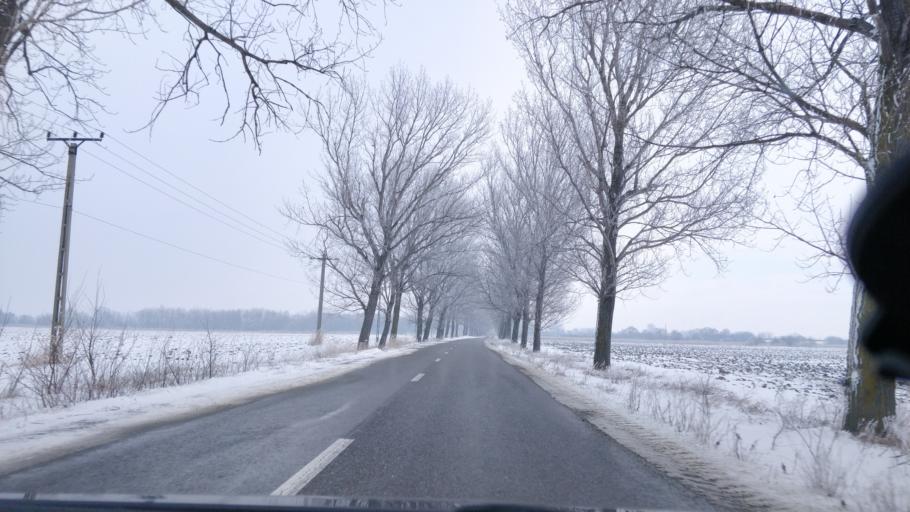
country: RO
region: Vrancea
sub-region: Comuna Vanatori
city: Jorasti
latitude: 45.6971
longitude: 27.2824
